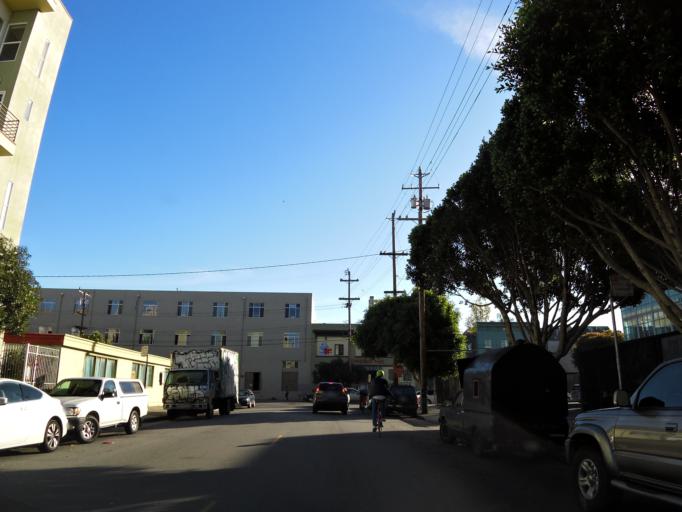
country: US
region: California
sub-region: San Francisco County
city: San Francisco
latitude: 37.7622
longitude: -122.4135
